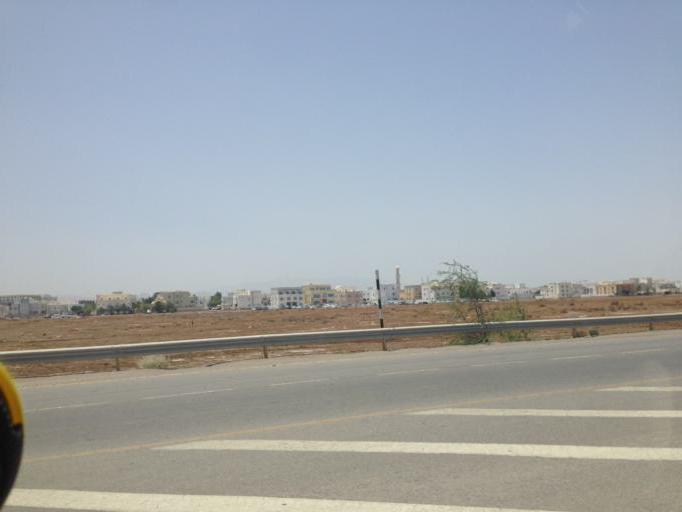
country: OM
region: Muhafazat Masqat
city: As Sib al Jadidah
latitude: 23.6267
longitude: 58.2610
